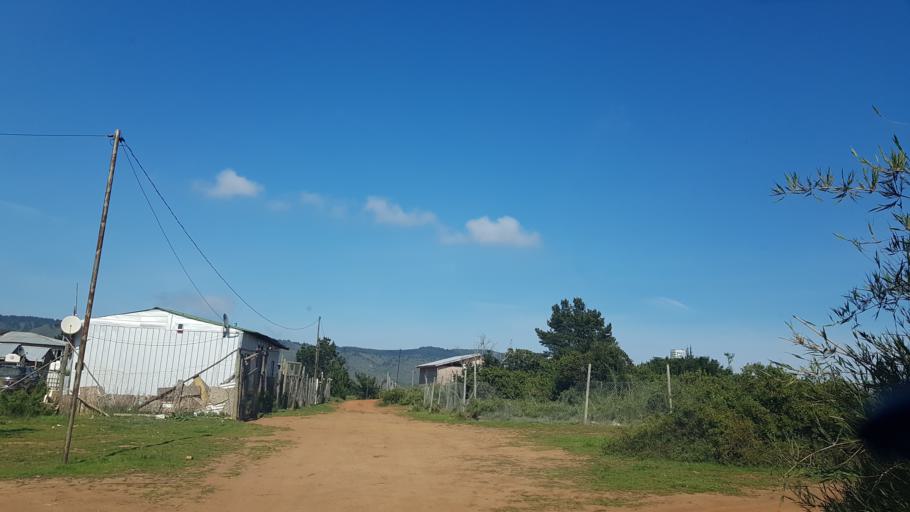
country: CL
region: Valparaiso
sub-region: Provincia de Valparaiso
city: Valparaiso
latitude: -33.1373
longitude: -71.6588
